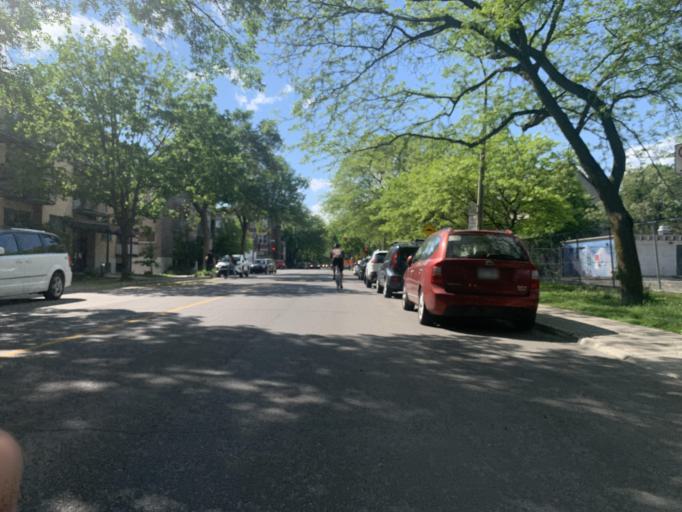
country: CA
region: Quebec
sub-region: Montreal
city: Montreal
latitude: 45.5347
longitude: -73.5642
